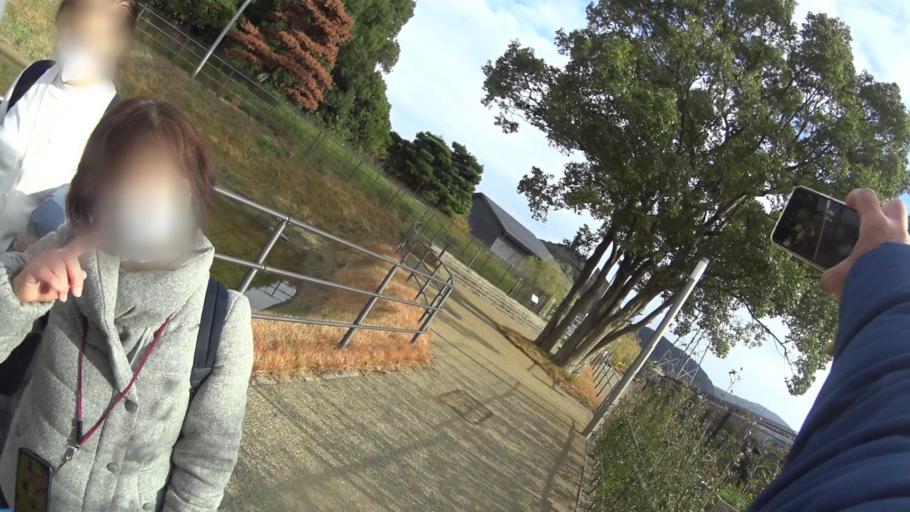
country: JP
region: Kyoto
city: Uji
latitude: 34.8971
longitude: 135.8043
